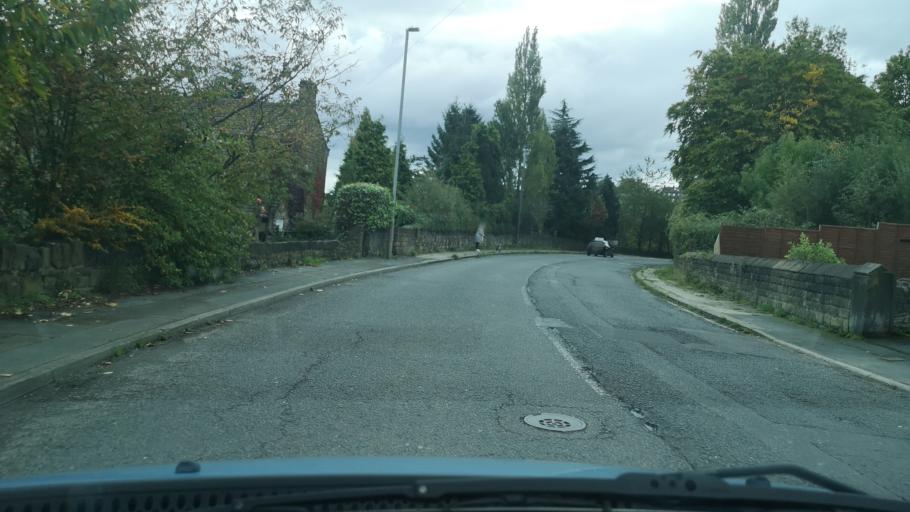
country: GB
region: England
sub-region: Kirklees
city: Dewsbury
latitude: 53.6698
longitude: -1.6208
